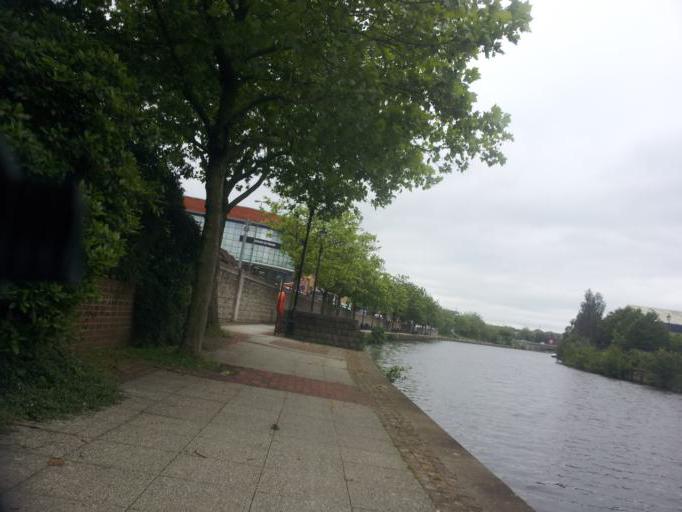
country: GB
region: England
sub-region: Kent
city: Maidstone
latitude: 51.2766
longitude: 0.5181
